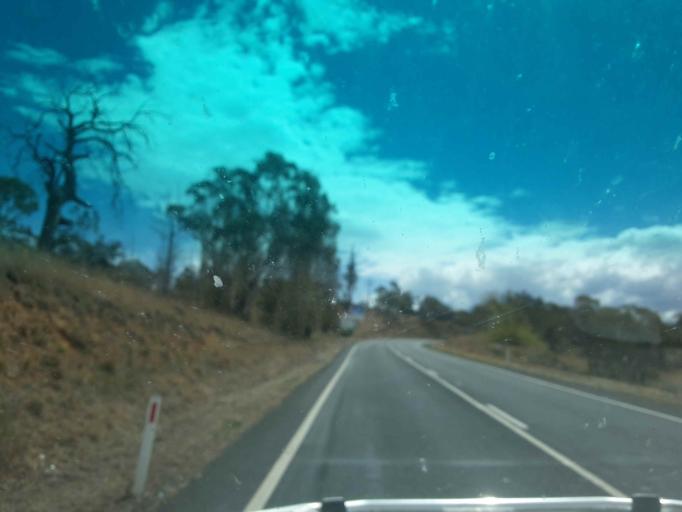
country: AU
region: New South Wales
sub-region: Snowy River
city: Jindabyne
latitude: -36.4266
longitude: 148.6214
